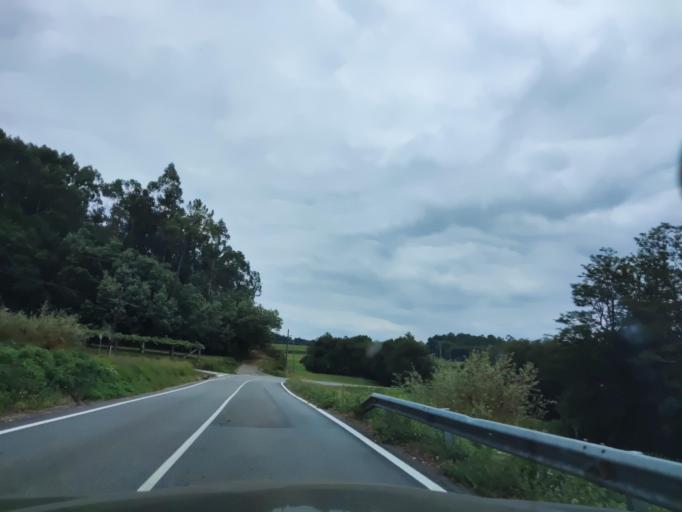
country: ES
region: Galicia
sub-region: Provincia da Coruna
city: Teo
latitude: 42.7595
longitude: -8.5589
